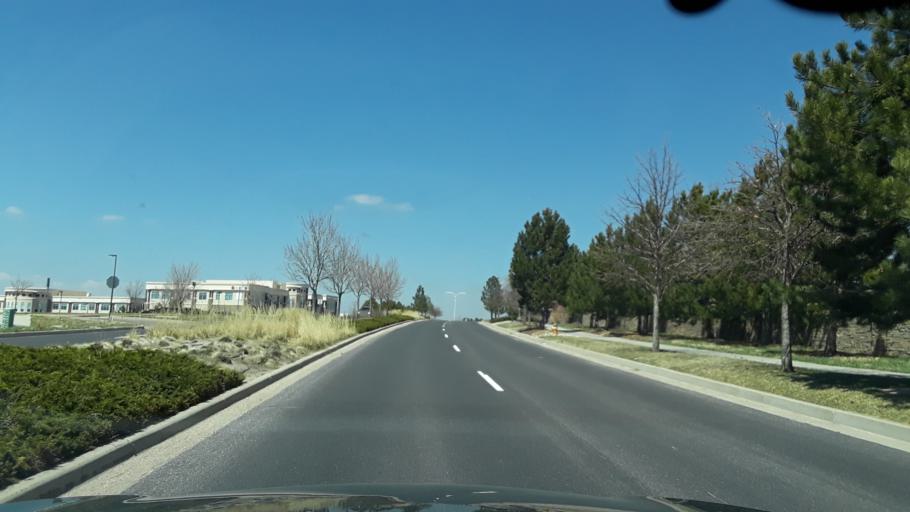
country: US
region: Colorado
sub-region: El Paso County
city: Black Forest
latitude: 38.9659
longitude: -104.7359
